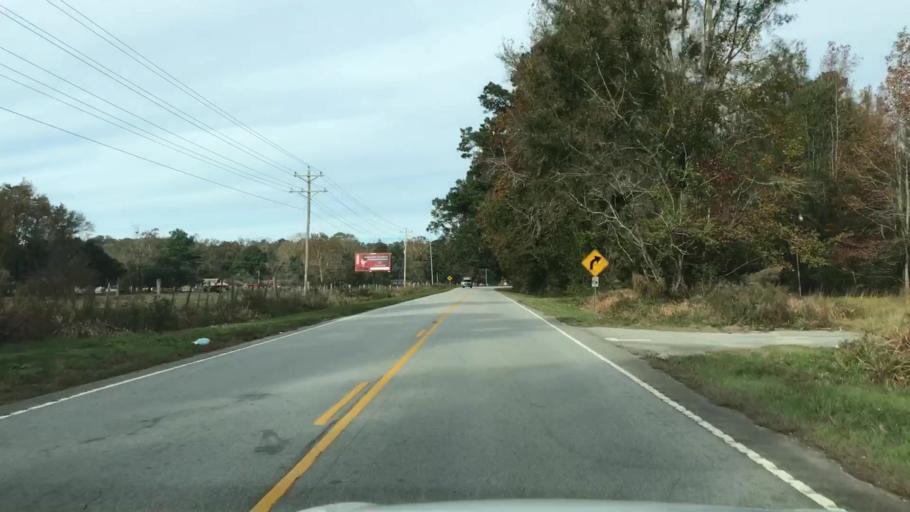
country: US
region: South Carolina
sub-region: Colleton County
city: Walterboro
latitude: 32.8220
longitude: -80.5540
